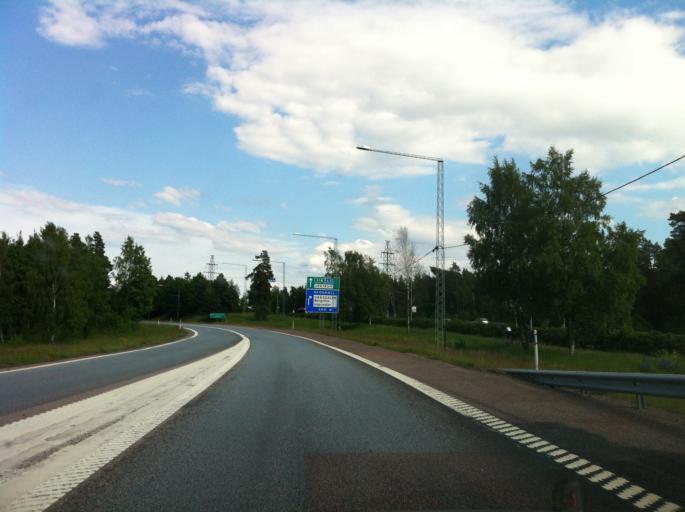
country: SE
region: Vaermland
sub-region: Hammaro Kommun
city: Skoghall
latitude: 59.3818
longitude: 13.4145
